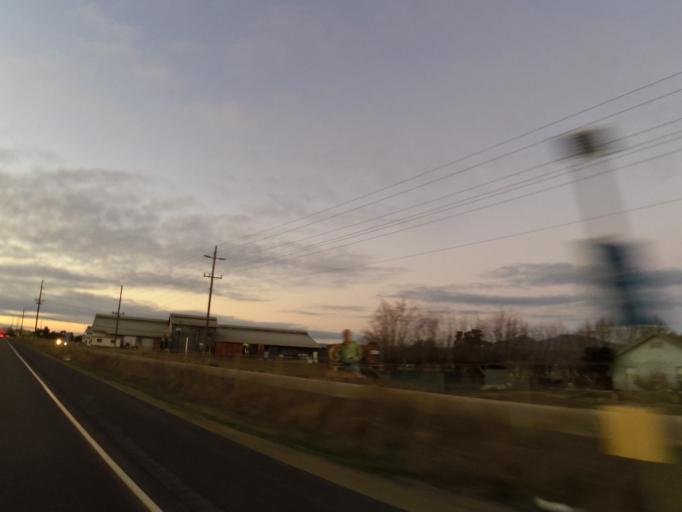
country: US
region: California
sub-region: Monterey County
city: Greenfield
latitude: 36.3078
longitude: -121.2278
